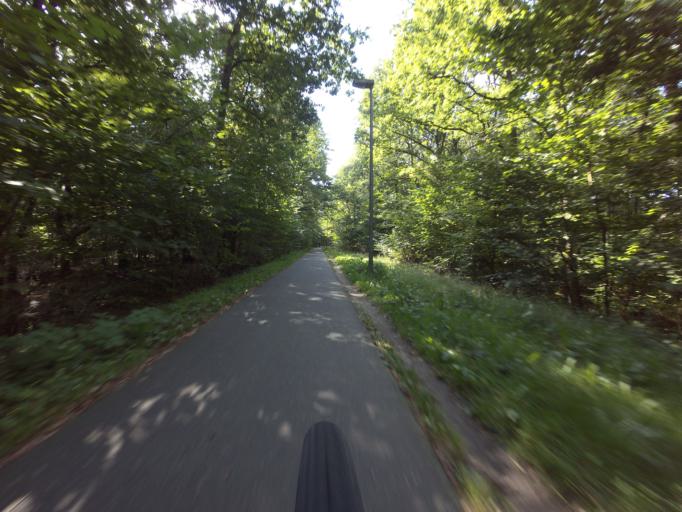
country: DK
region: Central Jutland
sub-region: Viborg Kommune
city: Viborg
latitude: 56.4041
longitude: 9.3566
